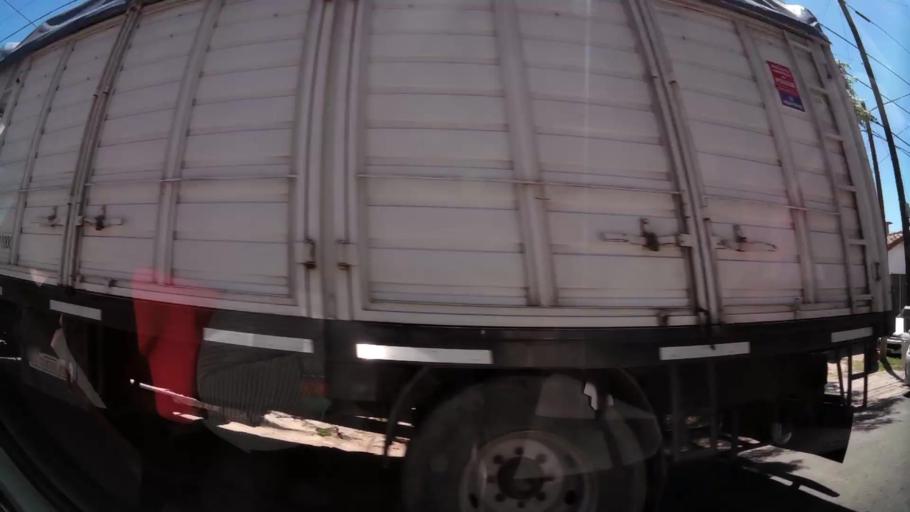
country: AR
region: Buenos Aires
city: Hurlingham
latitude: -34.5002
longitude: -58.6989
